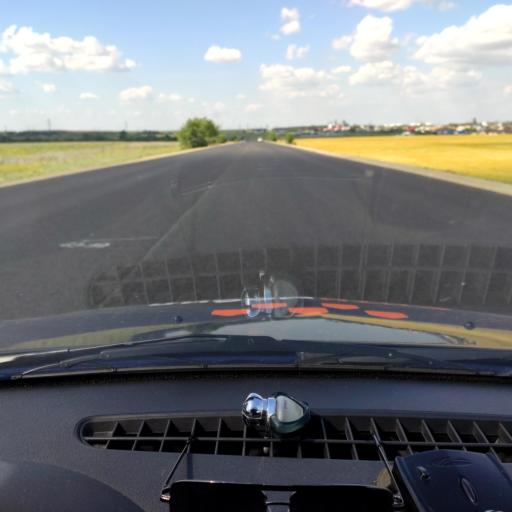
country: RU
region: Voronezj
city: Novovoronezh
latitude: 51.3480
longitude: 39.2775
